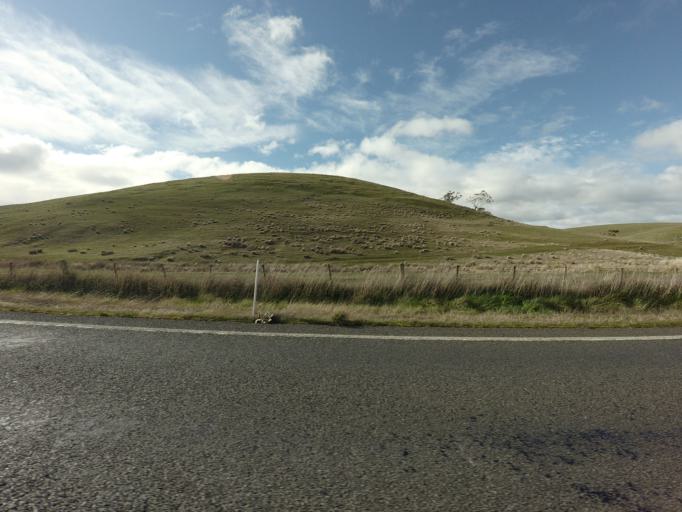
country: AU
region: Tasmania
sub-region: Derwent Valley
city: New Norfolk
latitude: -42.6099
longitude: 146.8856
